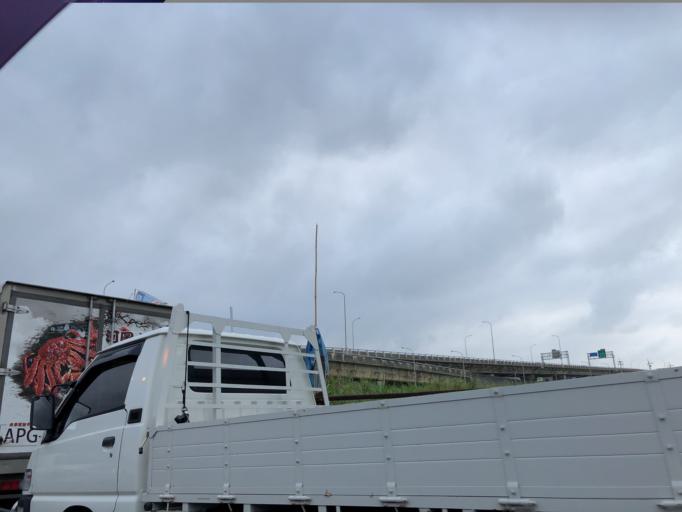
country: TW
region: Taiwan
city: Taoyuan City
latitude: 25.1132
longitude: 121.2431
